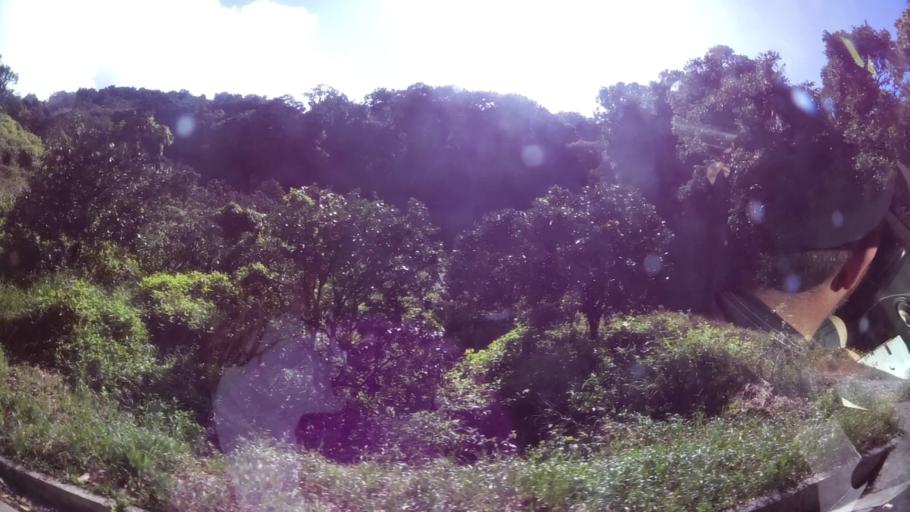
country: DM
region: Saint Paul
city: Pont Casse
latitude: 15.3701
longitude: -61.3510
